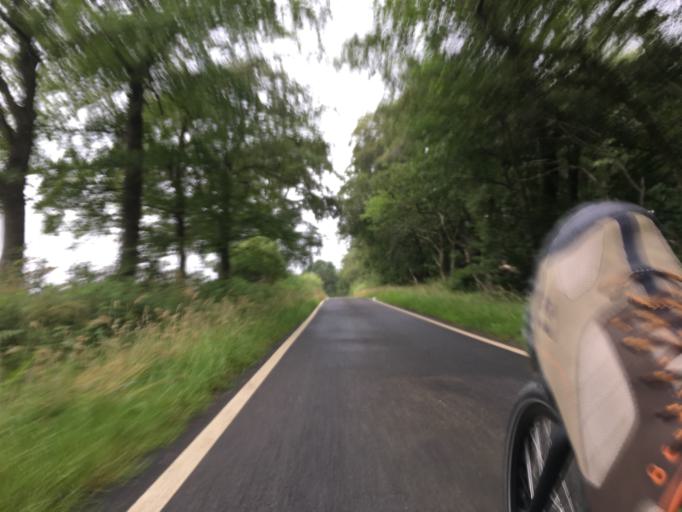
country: GB
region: Scotland
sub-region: West Lothian
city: West Calder
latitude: 55.8492
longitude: -3.5333
